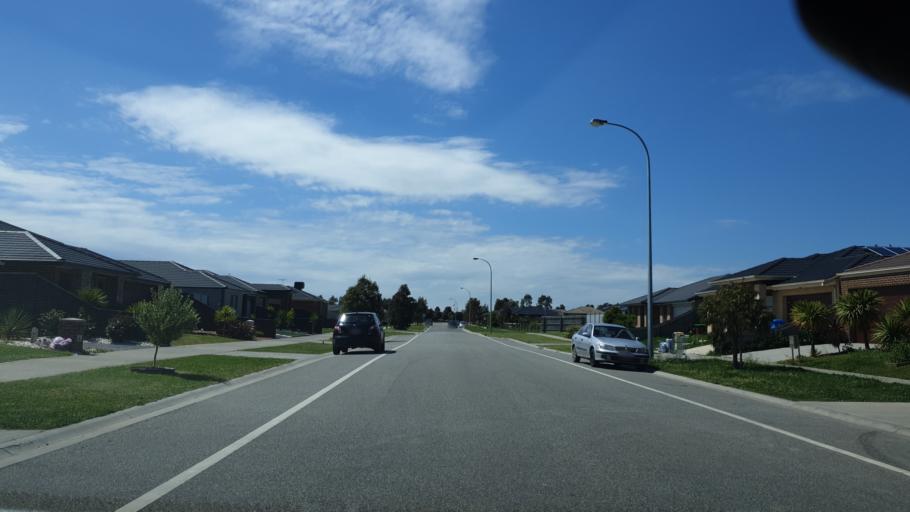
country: AU
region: Victoria
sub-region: Casey
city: Cranbourne East
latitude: -38.0974
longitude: 145.3088
